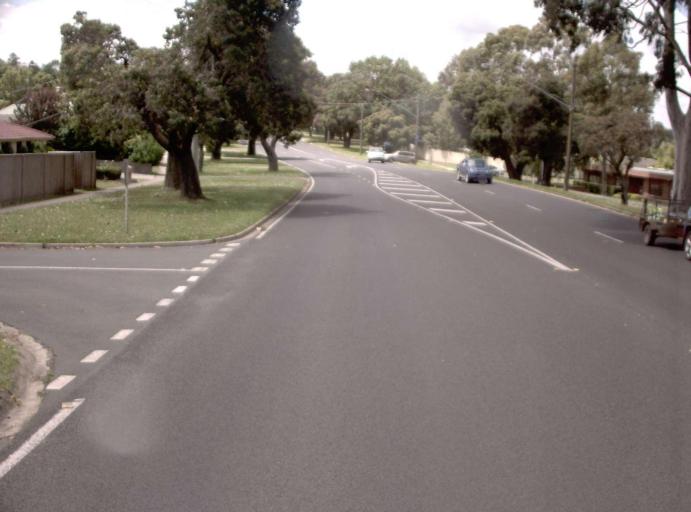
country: AU
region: Victoria
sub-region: Baw Baw
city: Warragul
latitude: -38.1294
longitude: 145.8488
